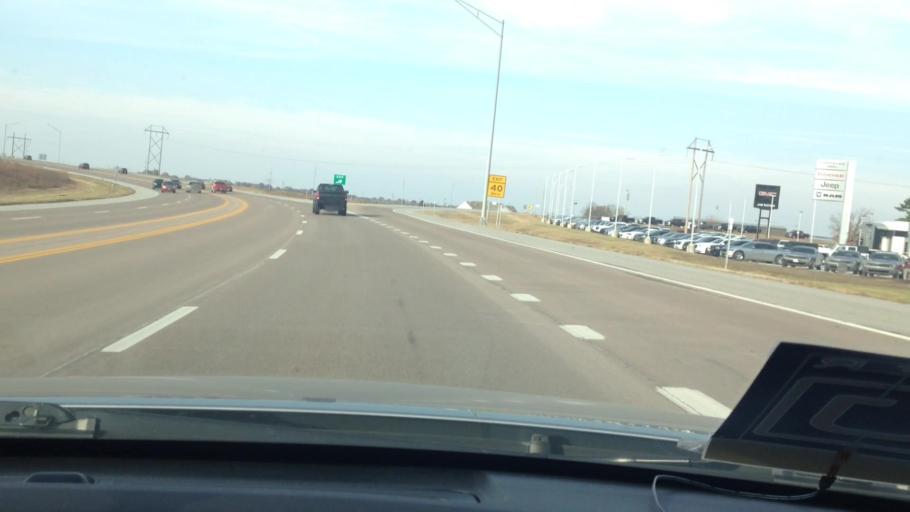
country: US
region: Missouri
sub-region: Henry County
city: Clinton
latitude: 38.3822
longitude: -93.7516
